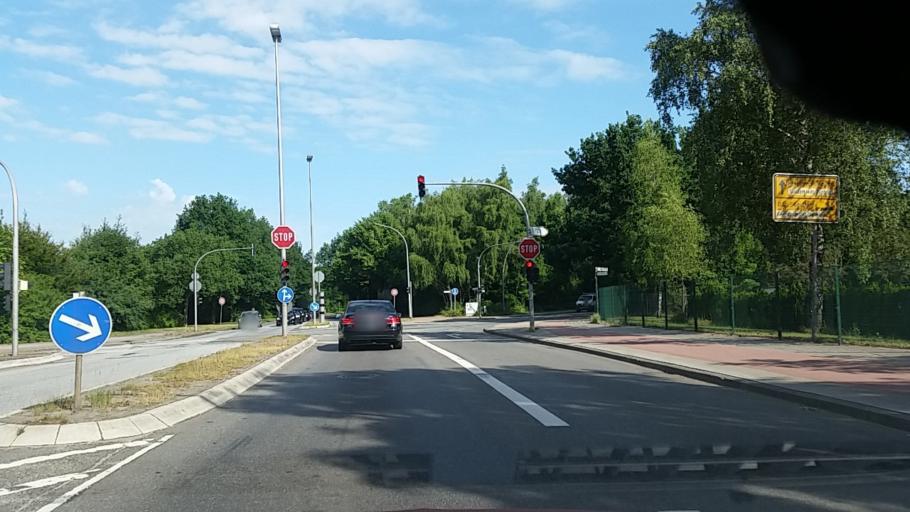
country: DE
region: Hamburg
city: Hummelsbuettel
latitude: 53.6803
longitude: 10.0470
